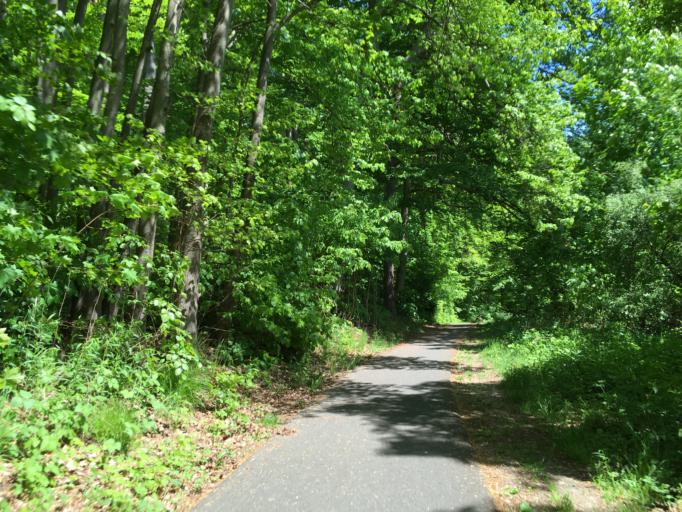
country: DE
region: Brandenburg
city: Chorin
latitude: 52.8516
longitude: 13.8675
